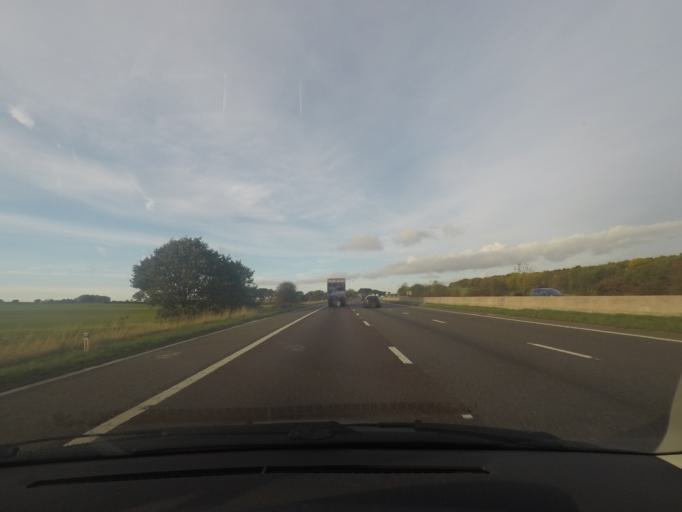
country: GB
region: England
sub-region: Barnsley
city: Darton
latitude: 53.6125
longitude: -1.5526
